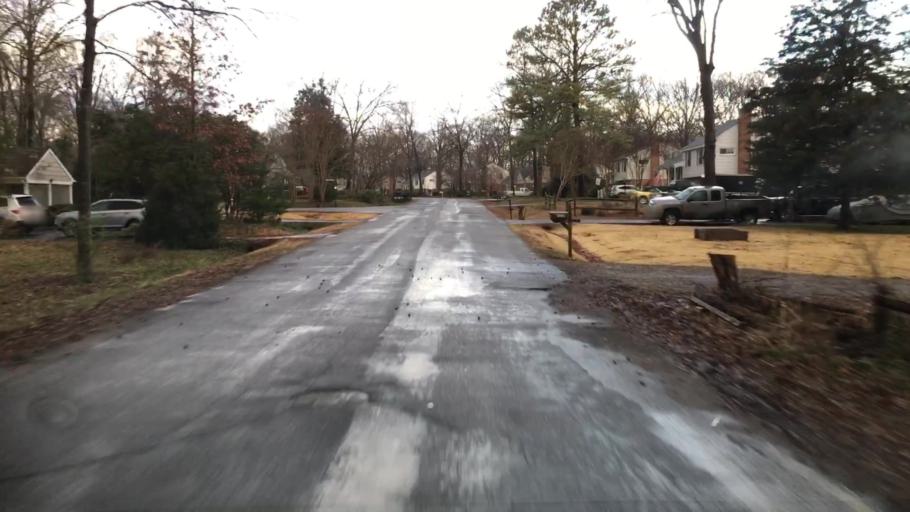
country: US
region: Virginia
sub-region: Chesterfield County
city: Bon Air
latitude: 37.5162
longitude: -77.6214
